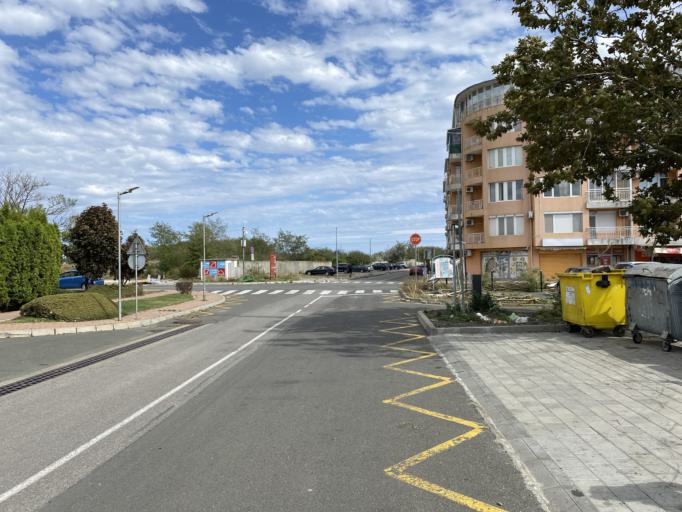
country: BG
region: Burgas
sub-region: Obshtina Pomorie
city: Pomorie
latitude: 42.5654
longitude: 27.6369
